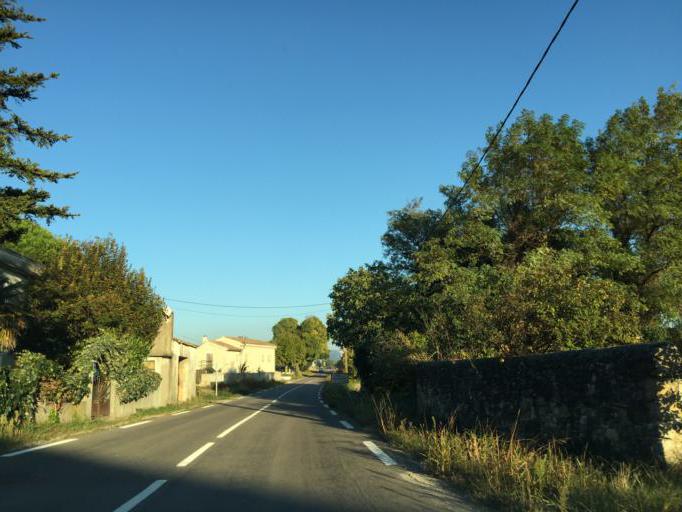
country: FR
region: Rhone-Alpes
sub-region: Departement de la Drome
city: Donzere
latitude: 44.4376
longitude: 4.6641
